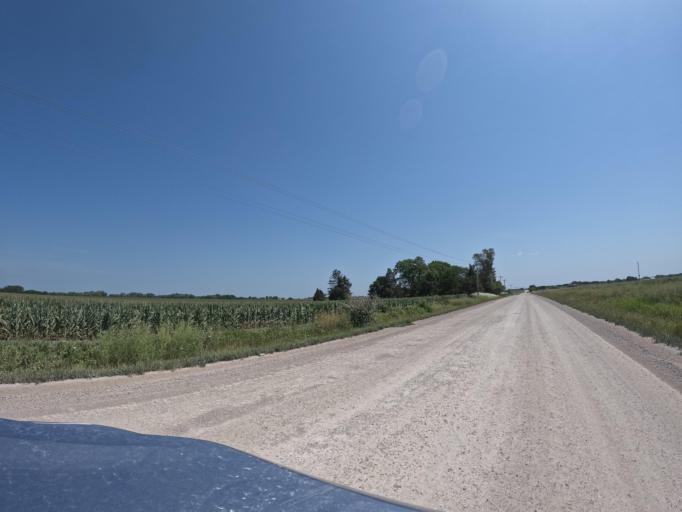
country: US
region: Iowa
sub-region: Henry County
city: Mount Pleasant
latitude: 40.9376
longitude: -91.5267
